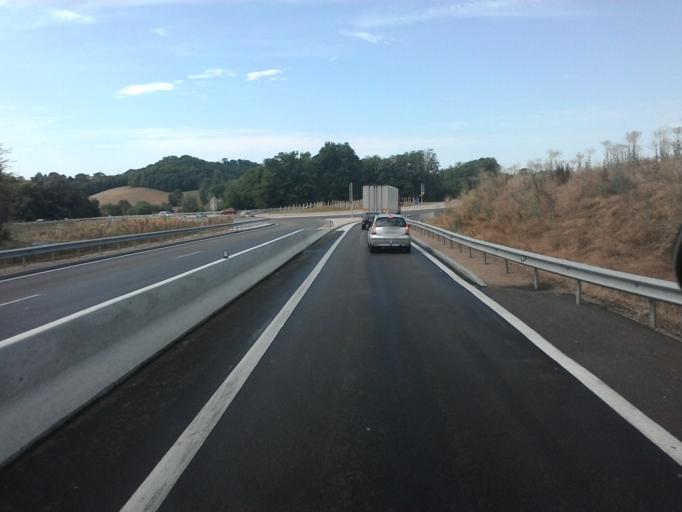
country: FR
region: Franche-Comte
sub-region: Departement du Jura
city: Lons-le-Saunier
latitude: 46.7083
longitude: 5.5499
